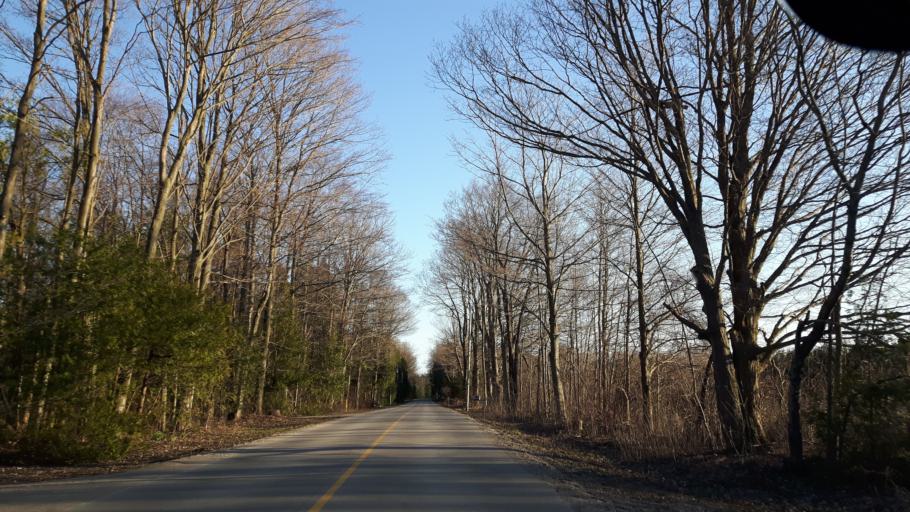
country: CA
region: Ontario
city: Bluewater
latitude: 43.5832
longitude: -81.6849
